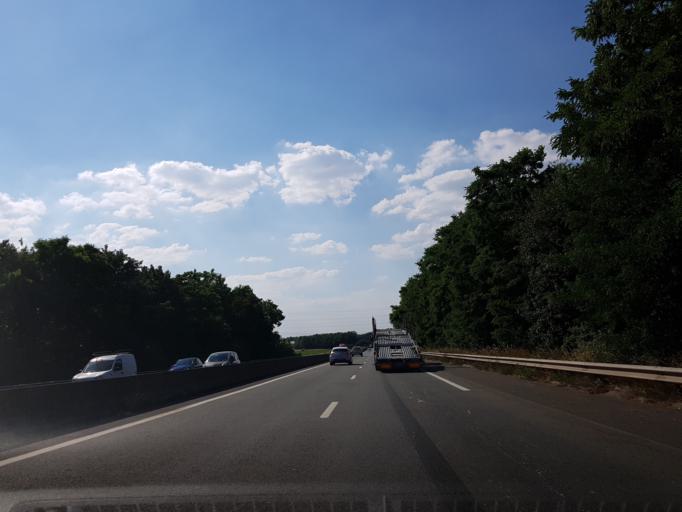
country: FR
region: Nord-Pas-de-Calais
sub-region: Departement du Nord
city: Escaudain
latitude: 50.3302
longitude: 3.3304
